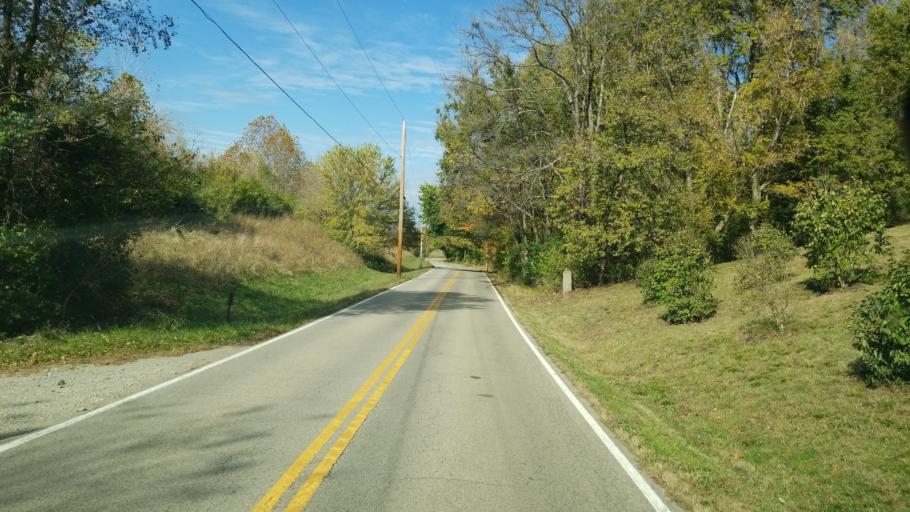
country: US
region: Ohio
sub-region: Warren County
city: Morrow
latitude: 39.3584
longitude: -84.1352
